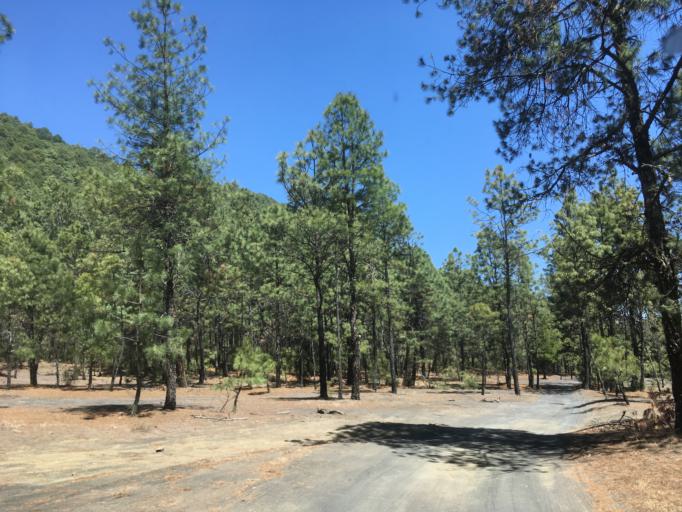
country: MX
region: Michoacan
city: Angahuan
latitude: 19.4653
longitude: -102.2399
